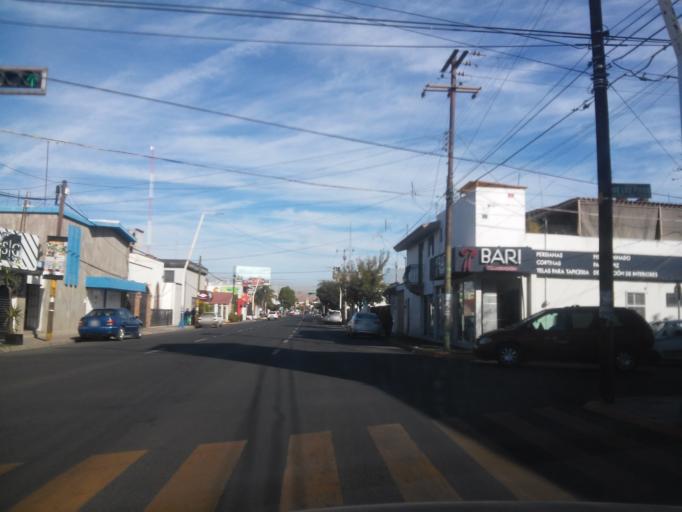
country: MX
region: Durango
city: Victoria de Durango
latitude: 24.0323
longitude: -104.6537
